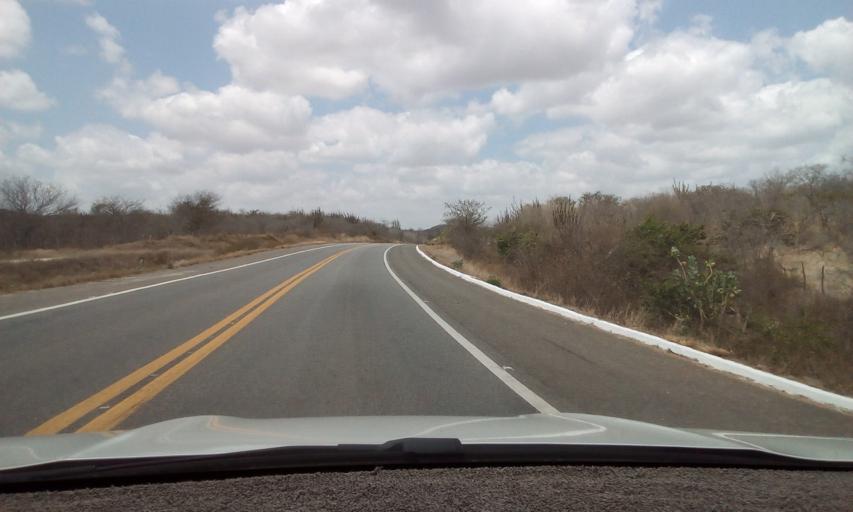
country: BR
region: Paraiba
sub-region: Boqueirao
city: Boqueirao
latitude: -7.6063
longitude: -36.0502
